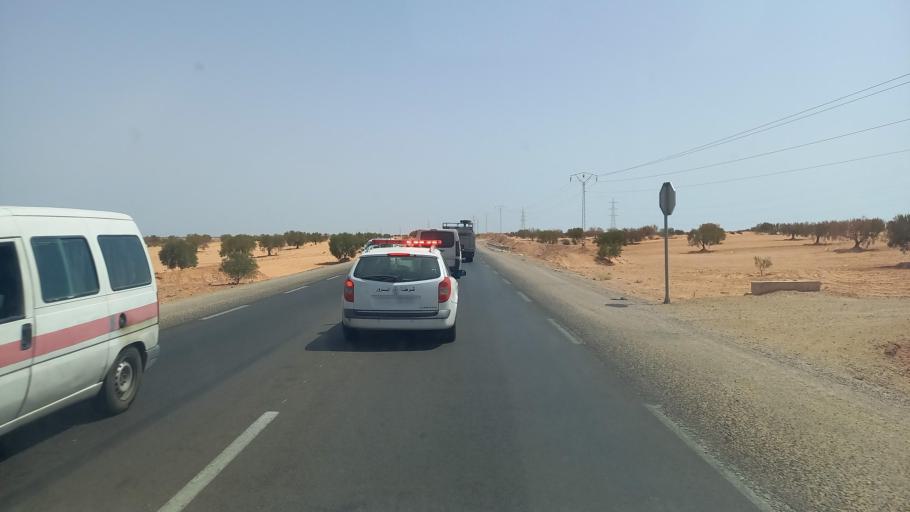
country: TN
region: Madanin
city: Zarzis
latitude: 33.4020
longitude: 10.8438
